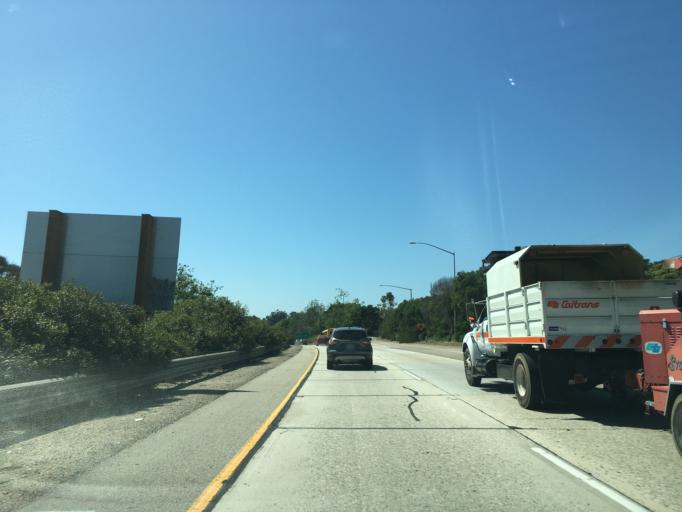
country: US
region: California
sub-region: Santa Barbara County
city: Montecito
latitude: 34.4223
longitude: -119.6369
